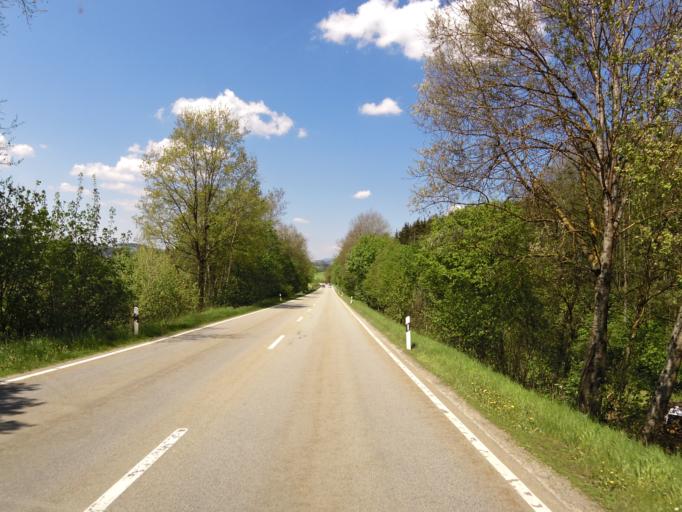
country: DE
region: Bavaria
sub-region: Lower Bavaria
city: Hutthurm
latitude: 48.6812
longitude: 13.4728
